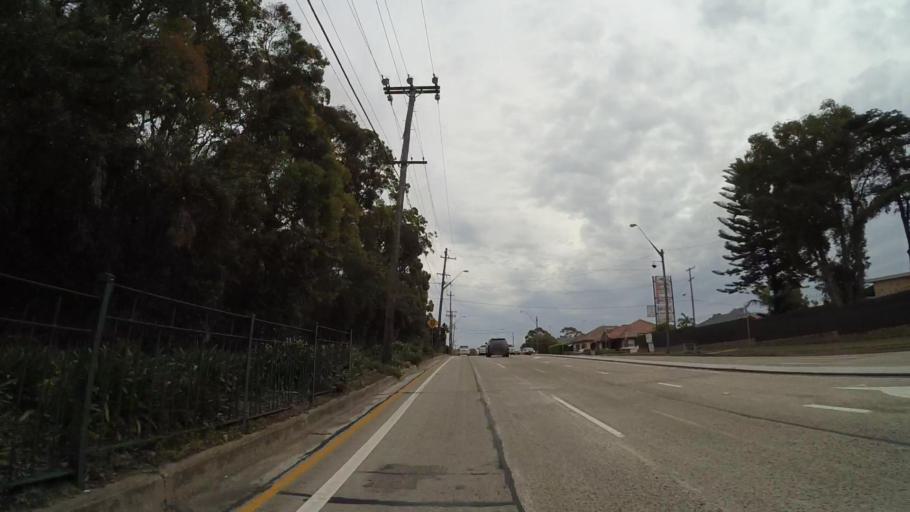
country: AU
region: New South Wales
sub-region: Kogarah
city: Kogarah
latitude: -33.9830
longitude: 151.1148
